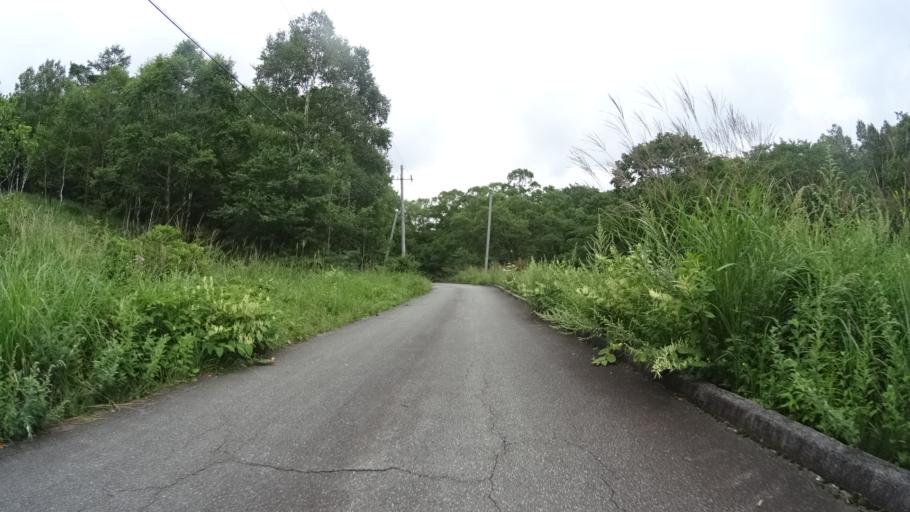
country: JP
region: Yamanashi
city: Enzan
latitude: 35.8001
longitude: 138.6349
